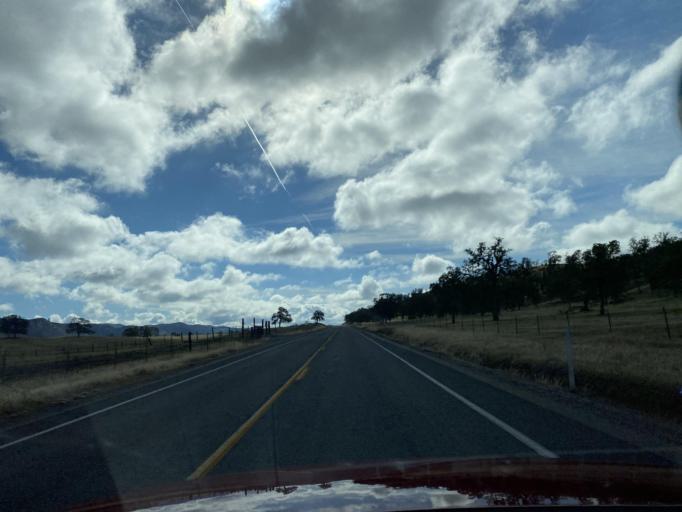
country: US
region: California
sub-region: Glenn County
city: Willows
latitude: 39.5383
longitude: -122.5352
